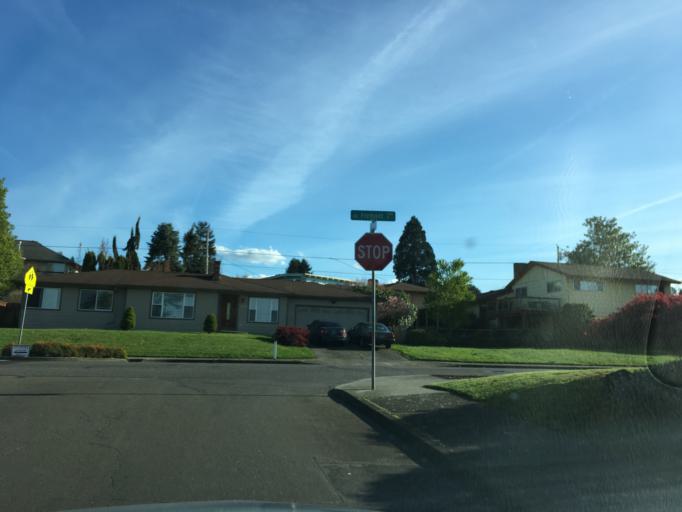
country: US
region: Oregon
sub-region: Multnomah County
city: Lents
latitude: 45.5483
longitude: -122.5274
